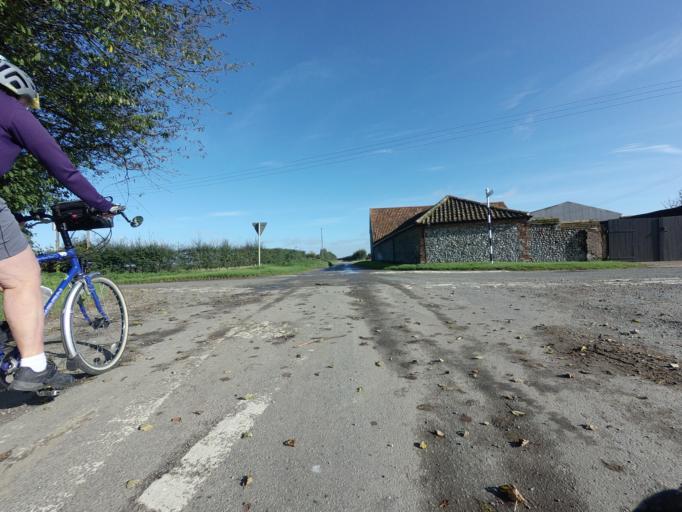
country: GB
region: England
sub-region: Norfolk
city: Dersingham
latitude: 52.8291
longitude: 0.6730
